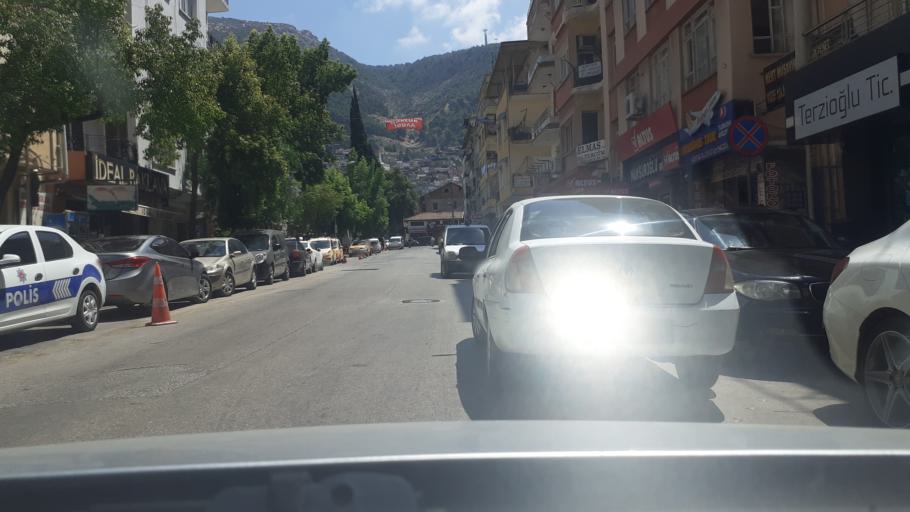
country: TR
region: Hatay
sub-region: Antakya Ilcesi
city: Antakya
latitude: 36.2018
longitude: 36.1641
